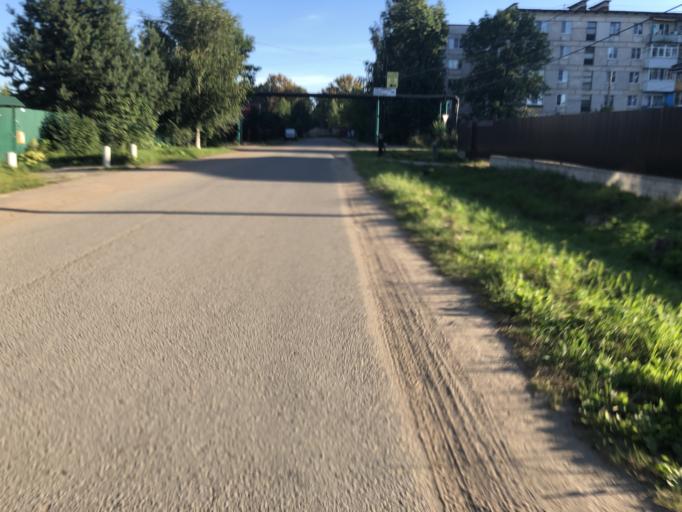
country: RU
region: Tverskaya
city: Rzhev
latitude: 56.2439
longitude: 34.3343
